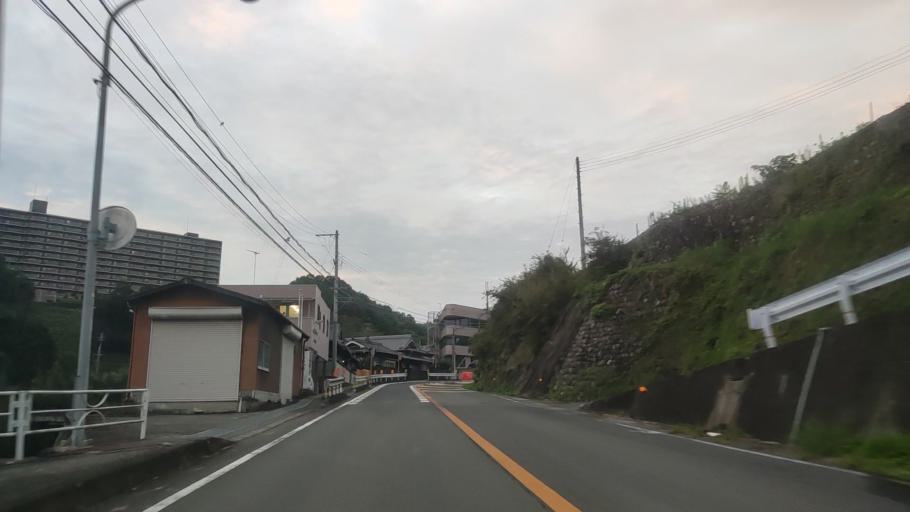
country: JP
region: Wakayama
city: Hashimoto
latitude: 34.3540
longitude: 135.6066
